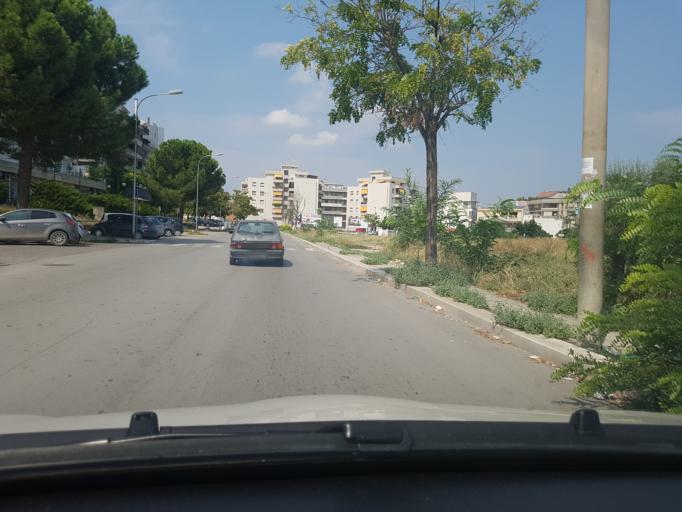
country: IT
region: Apulia
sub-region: Provincia di Foggia
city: Cerignola
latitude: 41.2661
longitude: 15.9083
